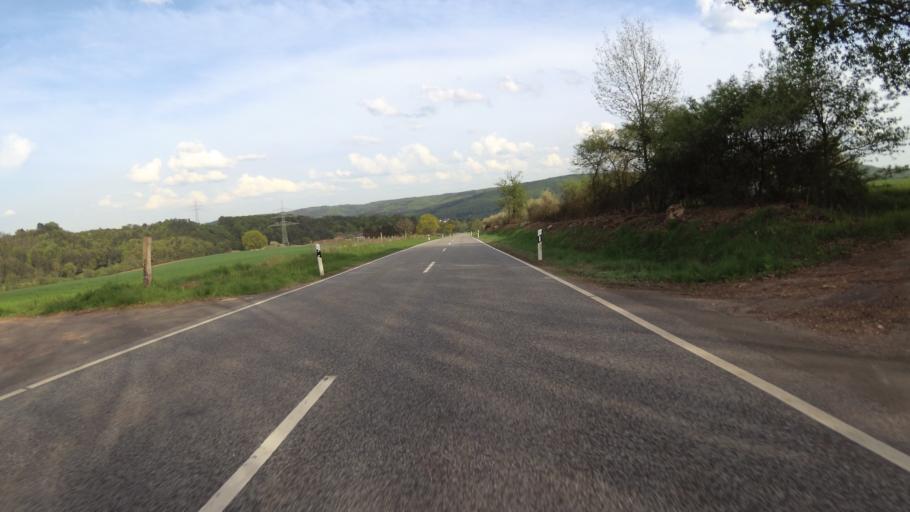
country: DE
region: Rheinland-Pfalz
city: Bausendorf
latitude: 50.0161
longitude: 7.0131
